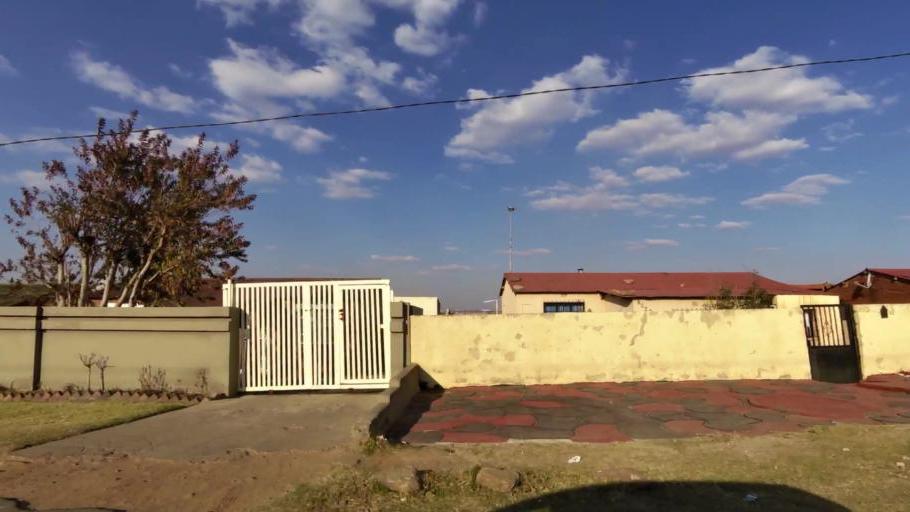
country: ZA
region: Gauteng
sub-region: City of Johannesburg Metropolitan Municipality
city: Soweto
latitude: -26.2329
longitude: 27.9036
